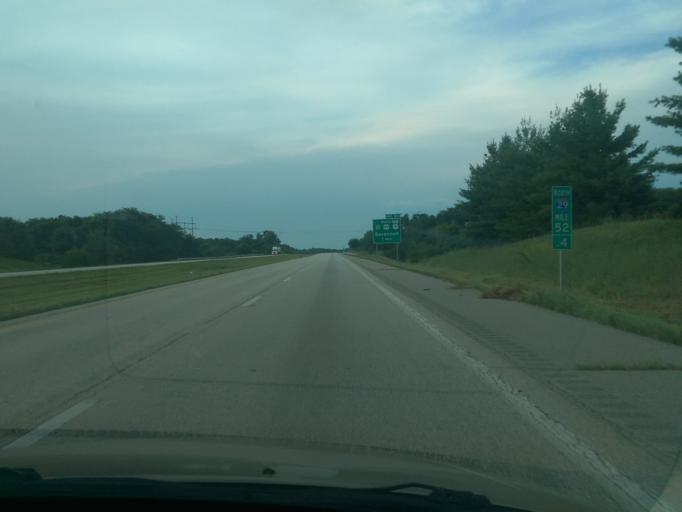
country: US
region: Missouri
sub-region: Andrew County
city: Country Club Village
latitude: 39.8398
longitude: -94.8053
